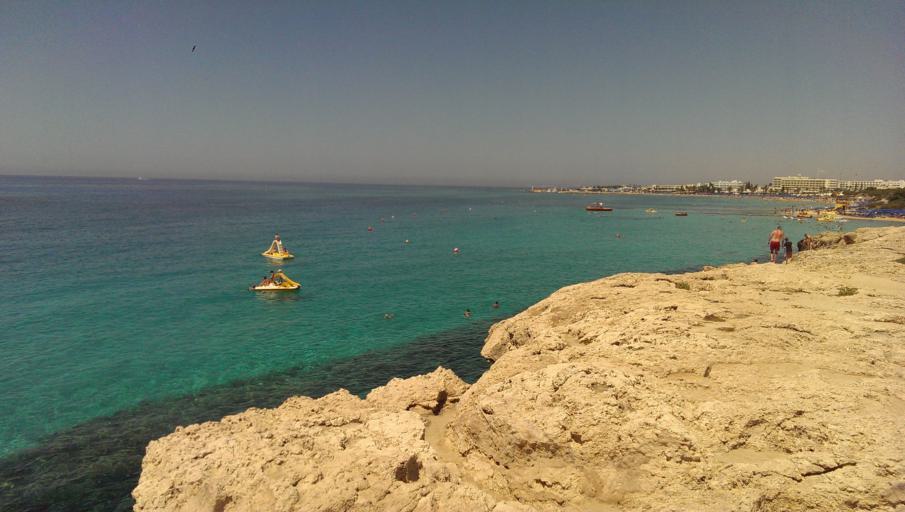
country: CY
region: Ammochostos
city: Ayia Napa
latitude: 34.9836
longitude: 34.0146
